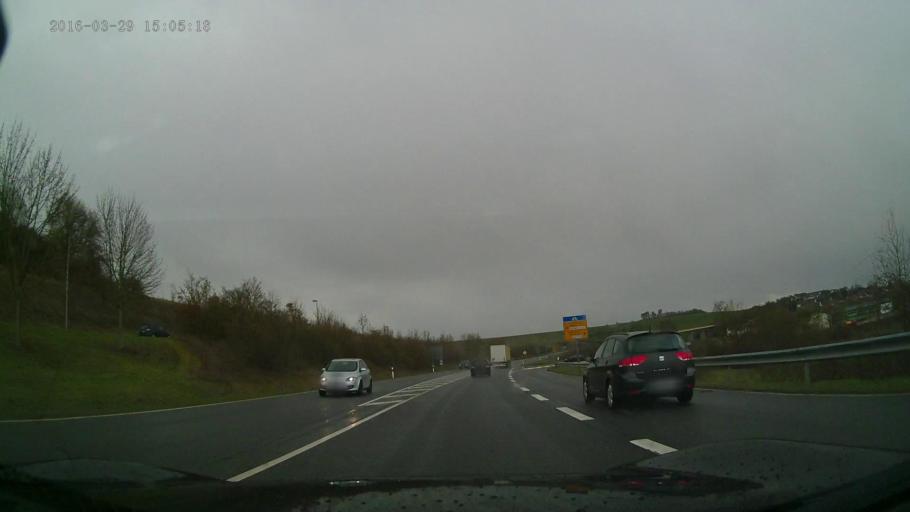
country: DE
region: Baden-Wuerttemberg
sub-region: Karlsruhe Region
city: Buchen
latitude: 49.5247
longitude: 9.3393
